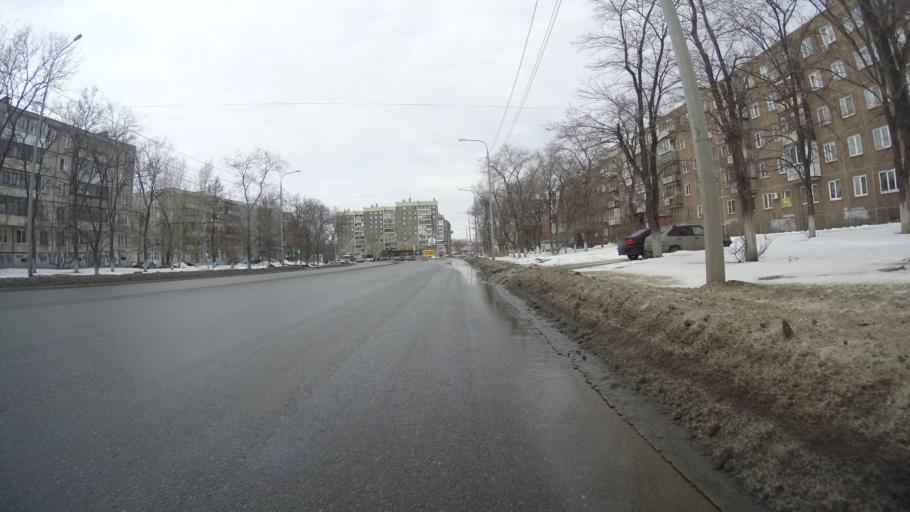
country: RU
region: Chelyabinsk
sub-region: Gorod Chelyabinsk
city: Chelyabinsk
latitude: 55.1967
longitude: 61.3329
